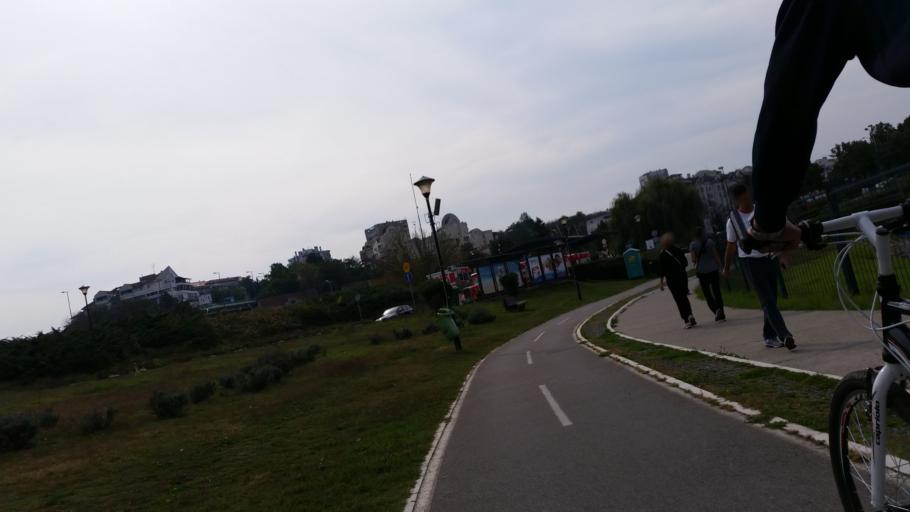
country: RS
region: Central Serbia
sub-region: Belgrade
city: Cukarica
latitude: 44.7886
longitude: 20.4155
